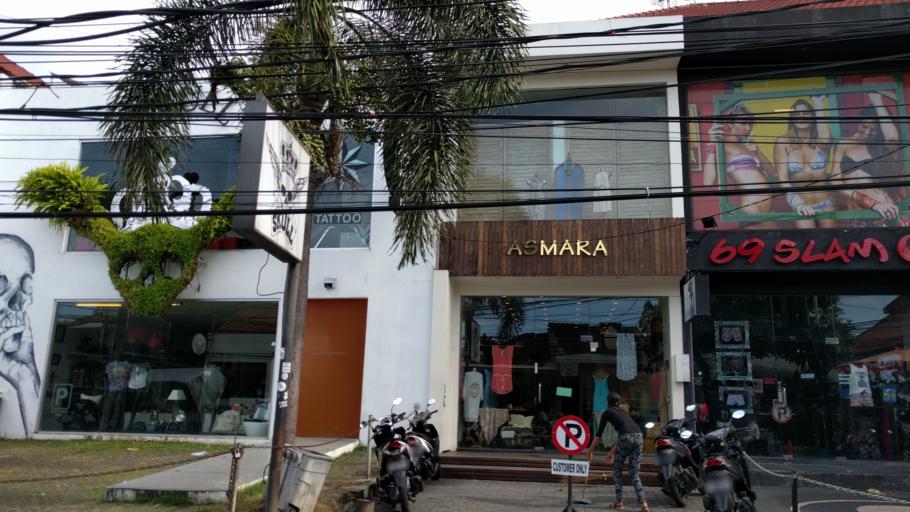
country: ID
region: Bali
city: Kuta
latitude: -8.6836
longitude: 115.1633
